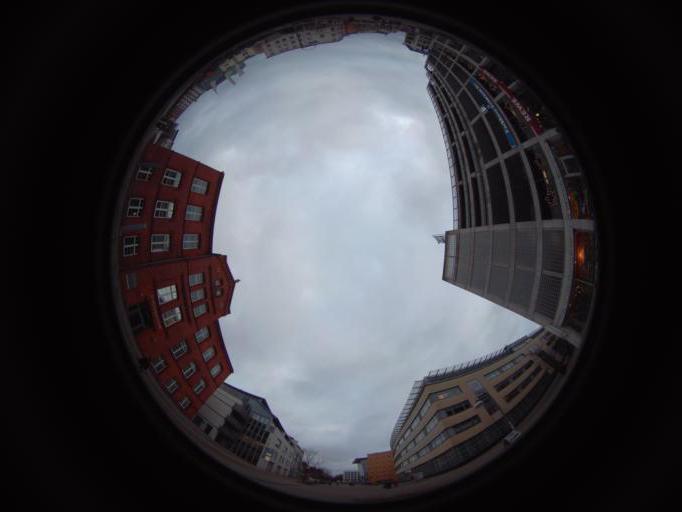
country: DE
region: Mecklenburg-Vorpommern
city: Rostock
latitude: 54.0871
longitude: 12.1246
